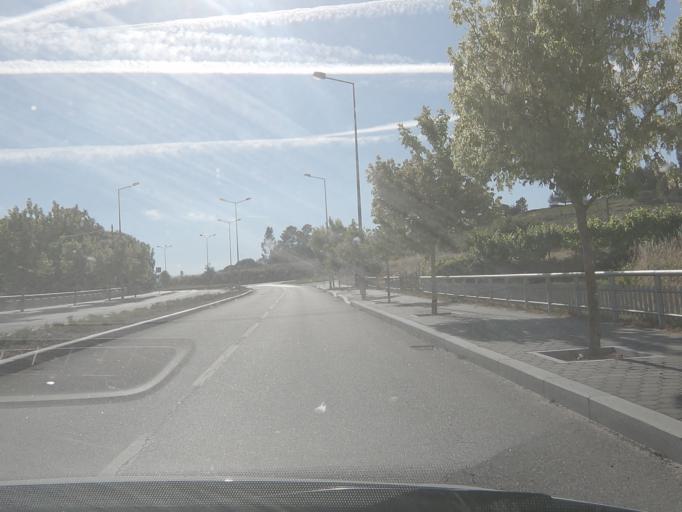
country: PT
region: Viseu
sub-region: Viseu
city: Viseu
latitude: 40.6683
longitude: -7.8954
